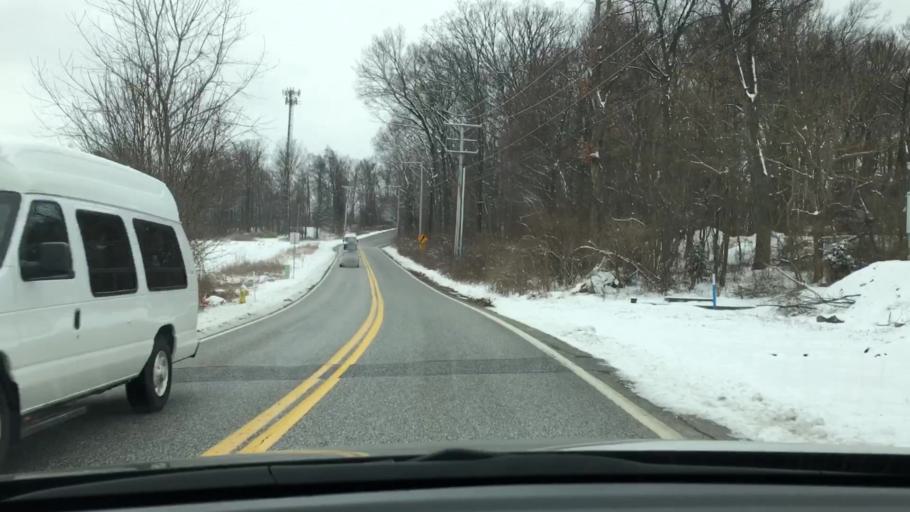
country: US
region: Pennsylvania
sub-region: York County
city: Grantley
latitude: 39.9240
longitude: -76.7205
